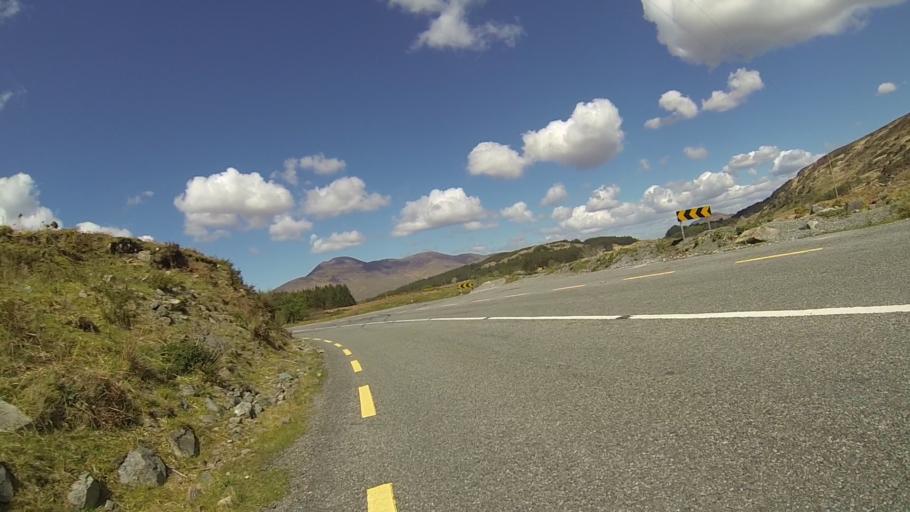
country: IE
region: Munster
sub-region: Ciarrai
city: Kenmare
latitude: 51.9519
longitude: -9.6266
